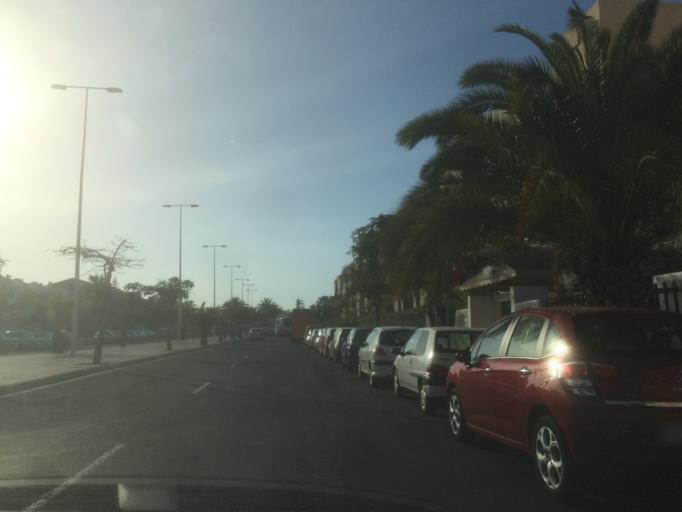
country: ES
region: Canary Islands
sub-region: Provincia de Santa Cruz de Tenerife
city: Playa de las Americas
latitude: 28.0884
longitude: -16.7334
